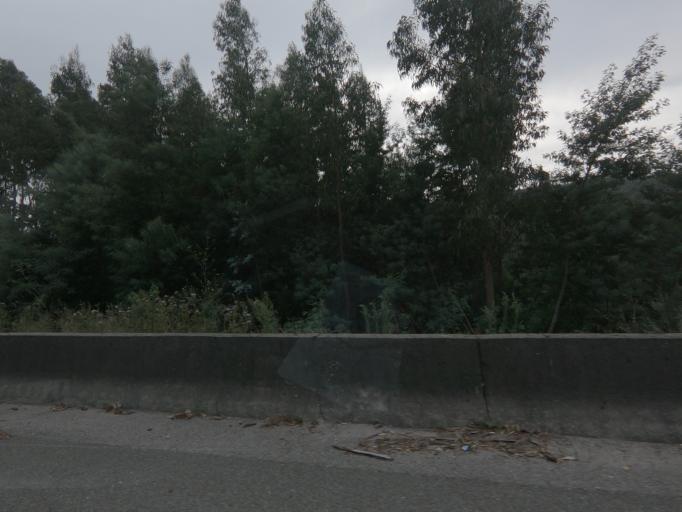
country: PT
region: Coimbra
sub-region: Penacova
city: Lorvao
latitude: 40.2955
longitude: -8.3094
